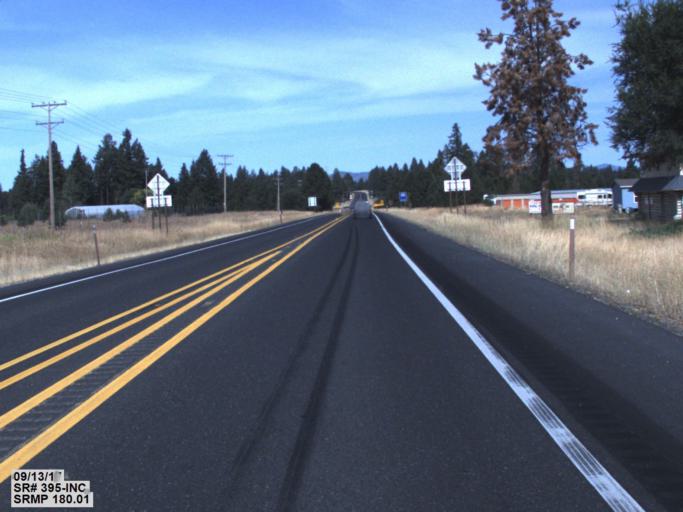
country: US
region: Washington
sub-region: Spokane County
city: Deer Park
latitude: 47.9485
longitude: -117.4829
